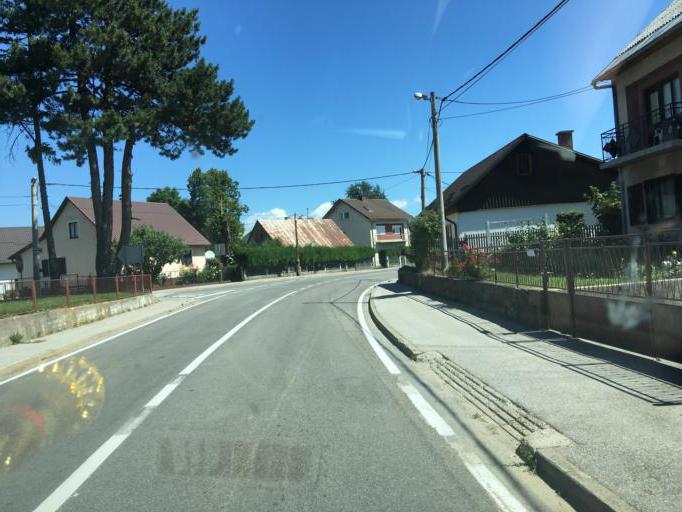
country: HR
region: Licko-Senjska
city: Gospic
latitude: 44.5419
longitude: 15.3507
